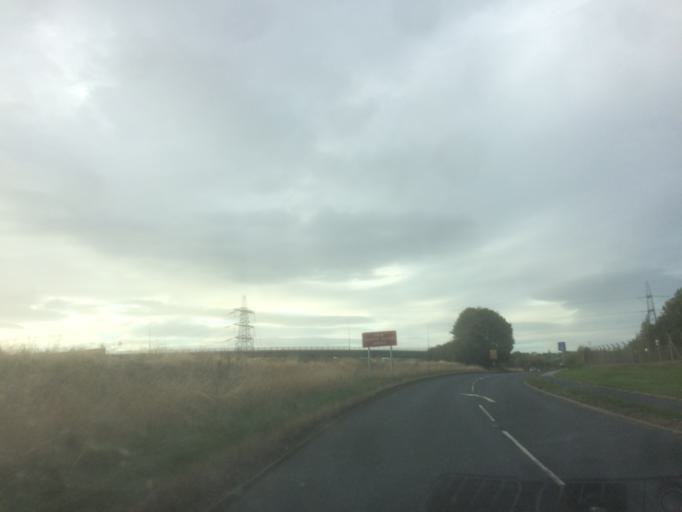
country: GB
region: England
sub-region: City and Borough of Wakefield
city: Ferrybridge
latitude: 53.7139
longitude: -1.2844
